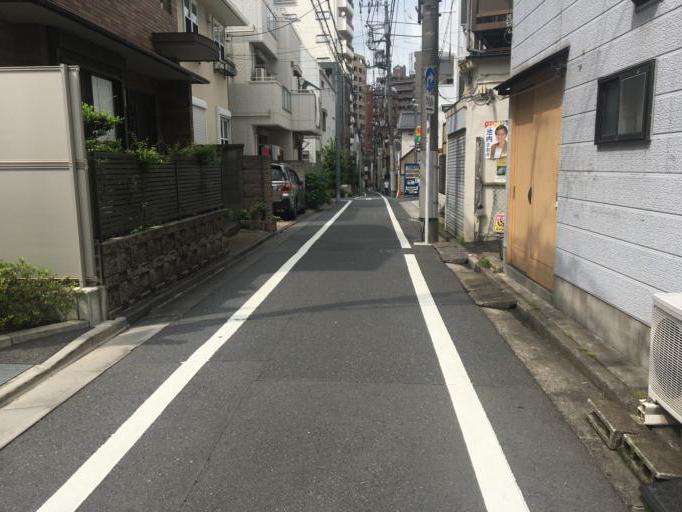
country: JP
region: Tokyo
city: Tokyo
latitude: 35.7348
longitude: 139.7193
